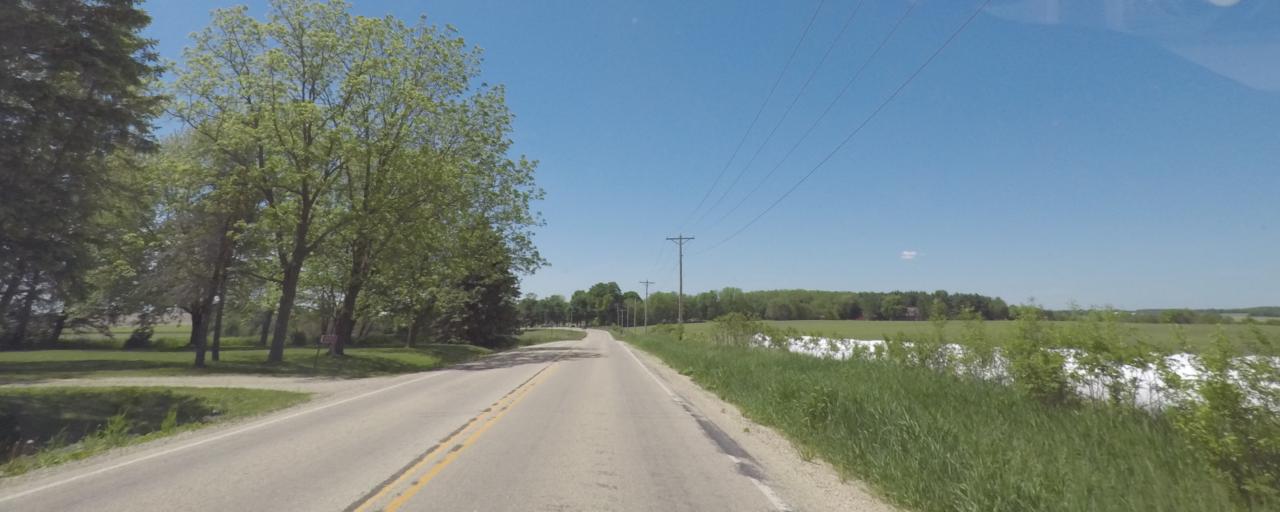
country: US
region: Wisconsin
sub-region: Rock County
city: Evansville
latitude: 42.7861
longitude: -89.3156
